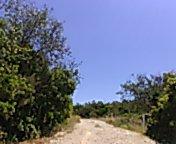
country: IT
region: Tuscany
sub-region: Provincia di Livorno
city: Capoliveri
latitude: 42.7468
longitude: 10.3194
